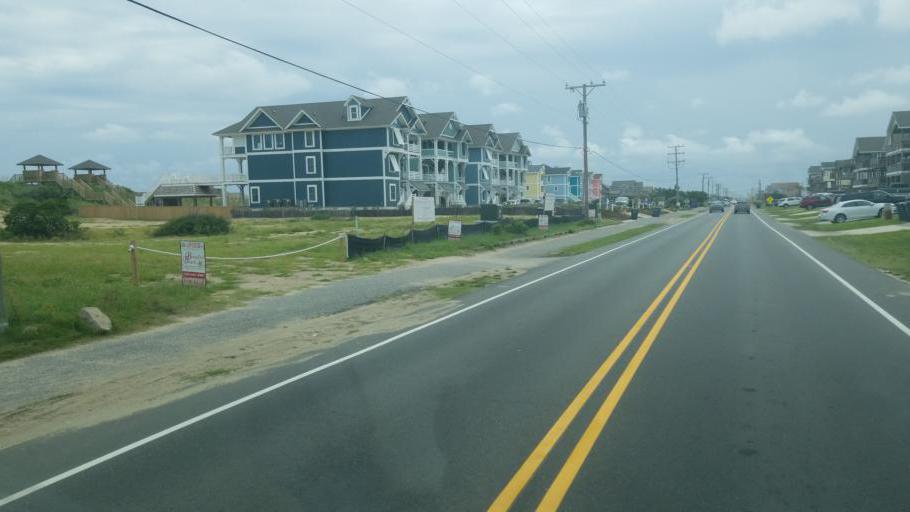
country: US
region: North Carolina
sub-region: Dare County
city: Nags Head
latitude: 35.9848
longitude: -75.6398
